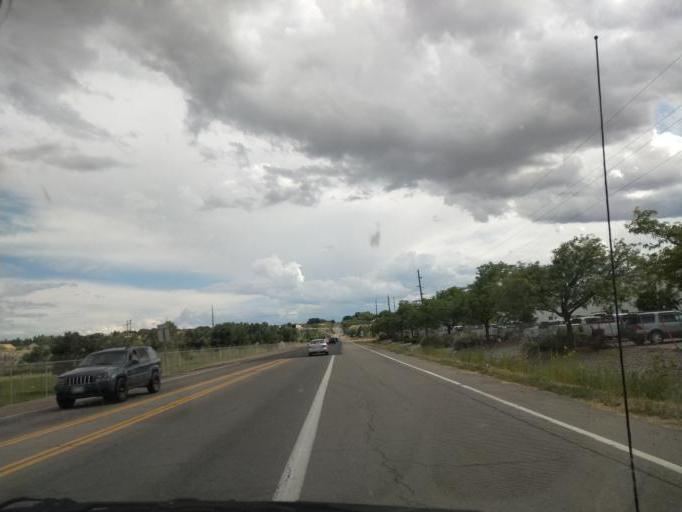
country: US
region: Colorado
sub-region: Mesa County
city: Clifton
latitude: 39.0609
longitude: -108.4595
